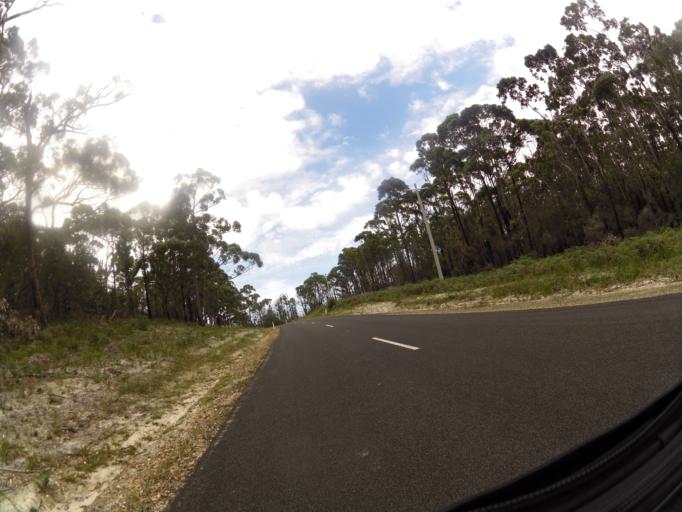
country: AU
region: Victoria
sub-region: East Gippsland
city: Lakes Entrance
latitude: -37.7821
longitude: 148.7301
